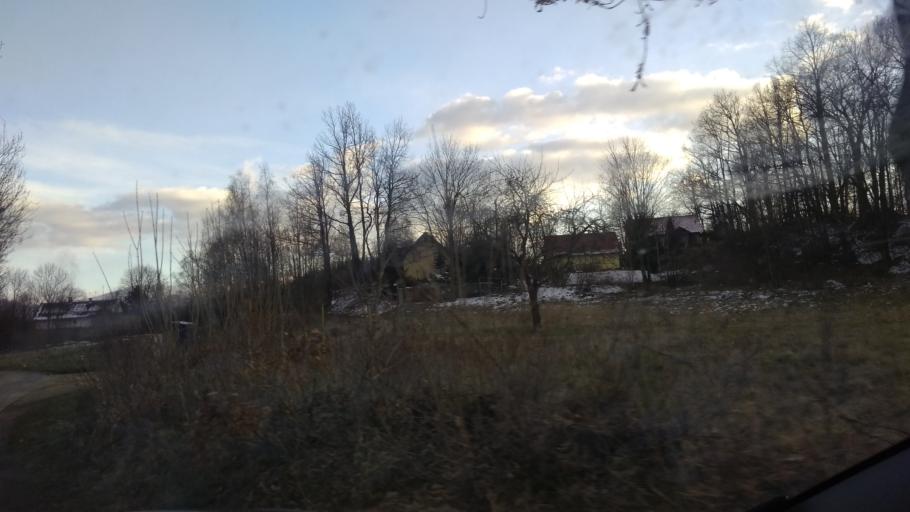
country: PL
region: Lower Silesian Voivodeship
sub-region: Powiat jeleniogorski
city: Sosnowka
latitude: 50.8447
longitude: 15.7380
